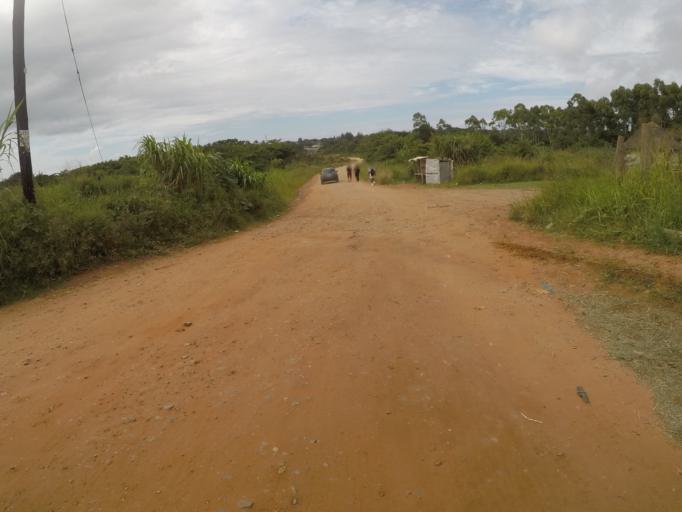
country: ZA
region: KwaZulu-Natal
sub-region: uThungulu District Municipality
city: eSikhawini
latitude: -28.8568
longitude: 31.9156
